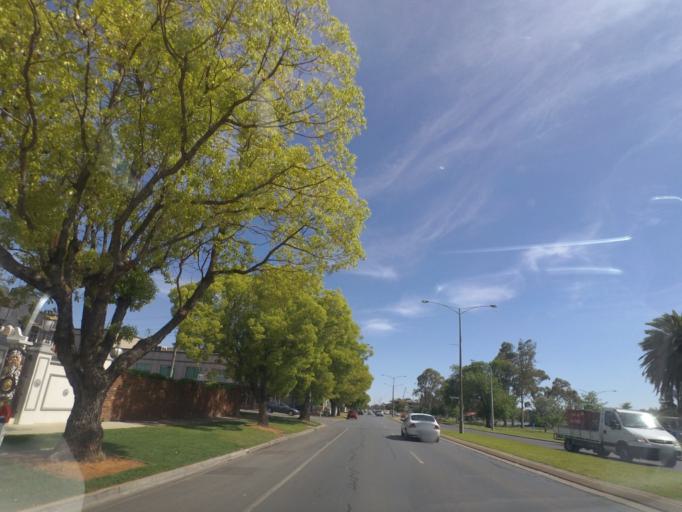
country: AU
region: Victoria
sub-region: Greater Shepparton
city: Shepparton
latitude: -36.3860
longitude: 145.3984
